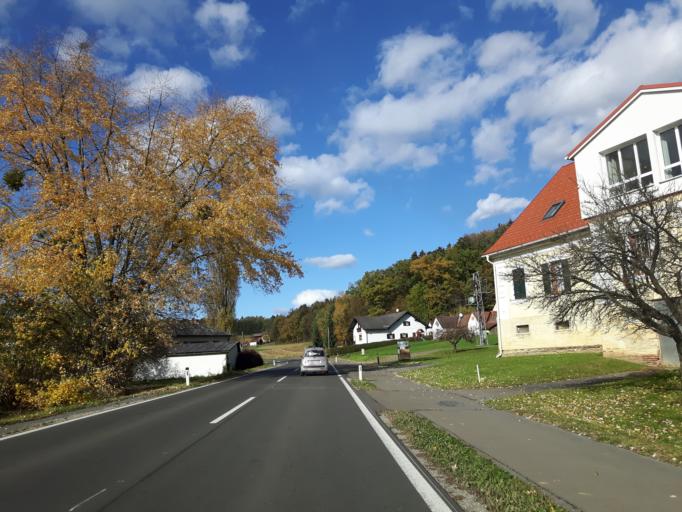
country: AT
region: Styria
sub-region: Politischer Bezirk Suedoststeiermark
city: Oberstorcha
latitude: 46.9514
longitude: 15.8306
